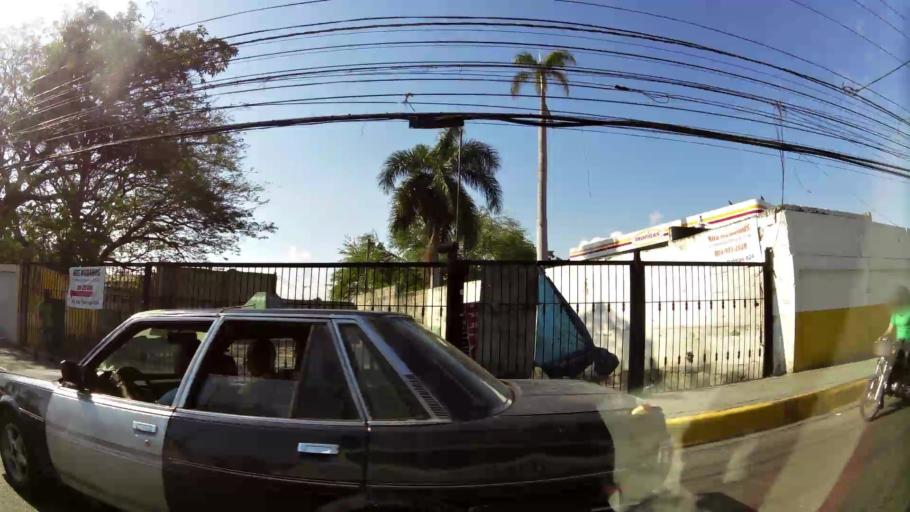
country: DO
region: Nacional
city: Santo Domingo
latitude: 18.4780
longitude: -69.9793
